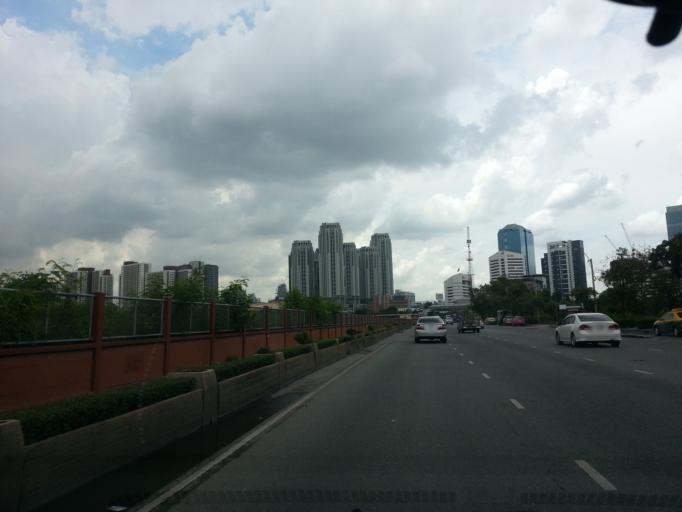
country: TH
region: Bangkok
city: Huai Khwang
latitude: 13.7637
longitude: 100.5766
